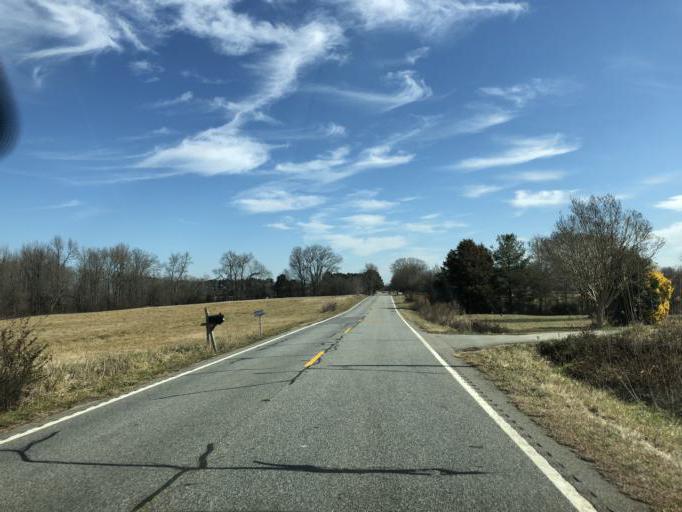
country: US
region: South Carolina
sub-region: Spartanburg County
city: Boiling Springs
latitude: 35.0510
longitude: -81.9199
